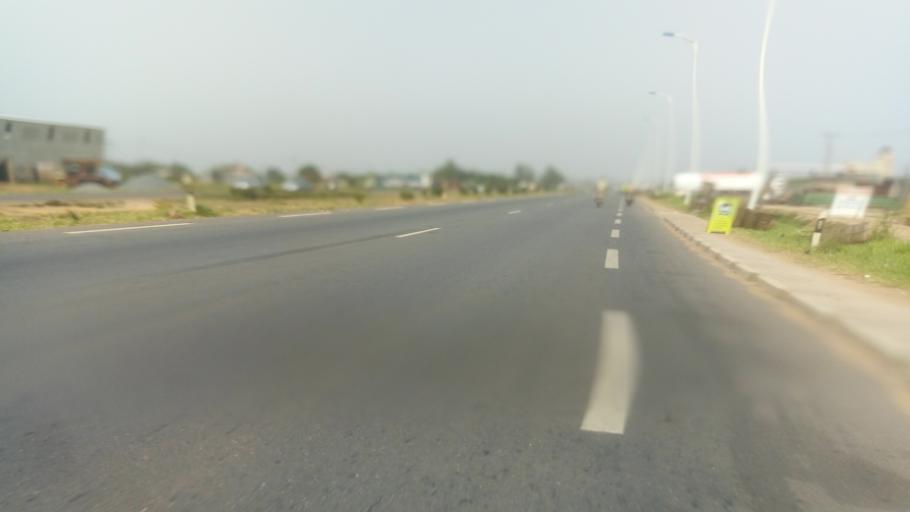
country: TG
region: Maritime
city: Tsevie
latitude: 6.2966
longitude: 1.2139
